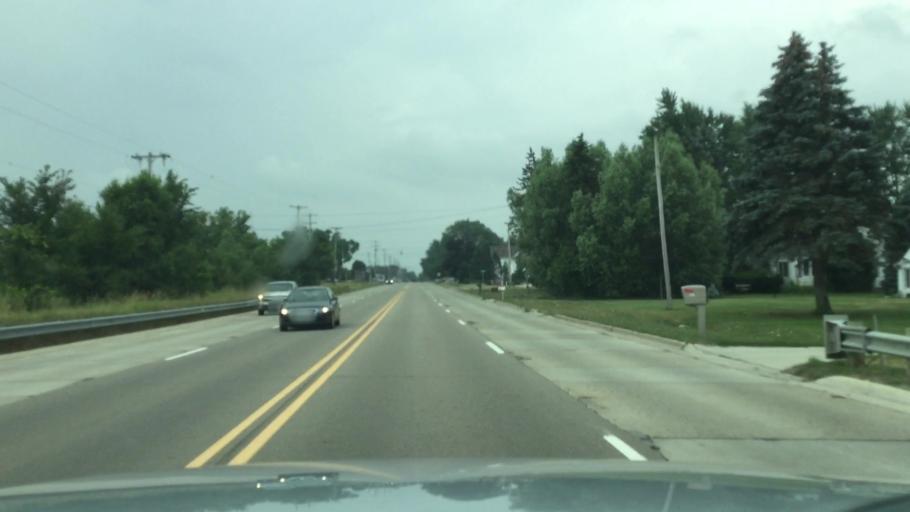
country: US
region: Michigan
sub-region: Shiawassee County
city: Owosso
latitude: 43.0225
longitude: -84.1769
